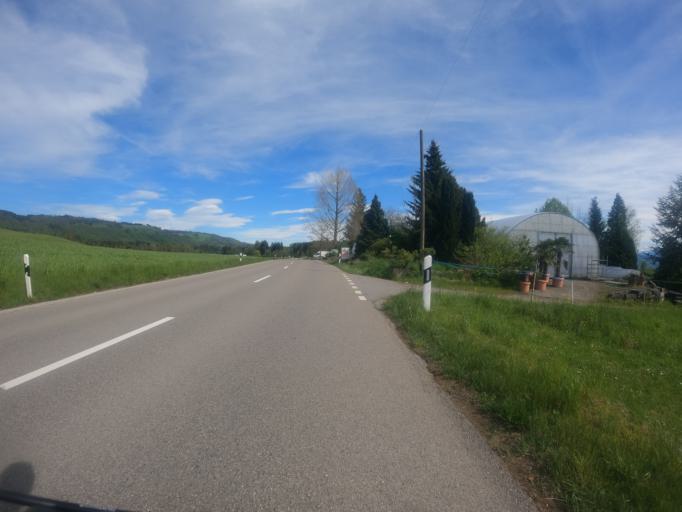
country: CH
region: Zurich
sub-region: Bezirk Affoltern
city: Hausen am Albis / Hausen (Dorf)
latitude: 47.2396
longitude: 8.5020
